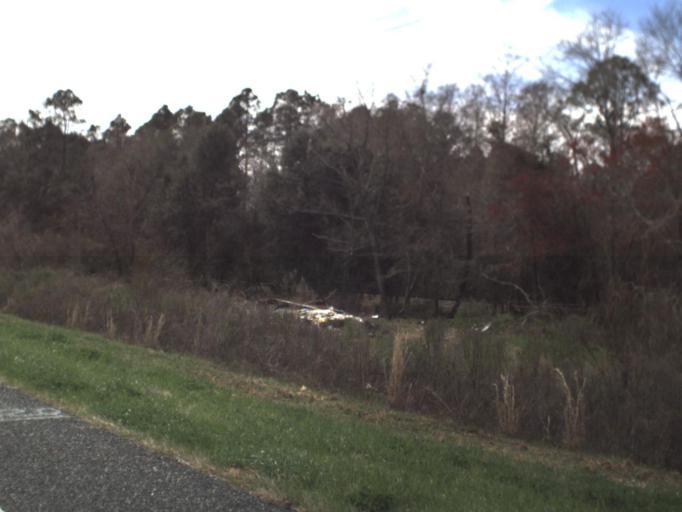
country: US
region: Florida
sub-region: Washington County
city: Chipley
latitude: 30.7213
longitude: -85.3896
